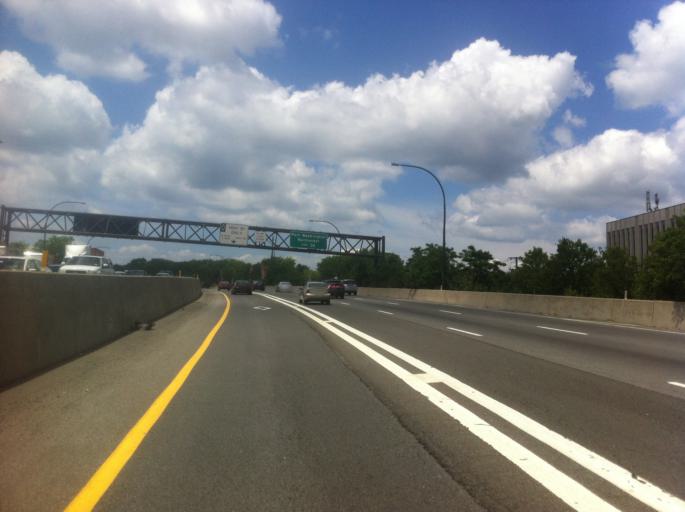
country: US
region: New York
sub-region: Nassau County
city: Roslyn Heights
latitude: 40.7848
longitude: -73.6385
